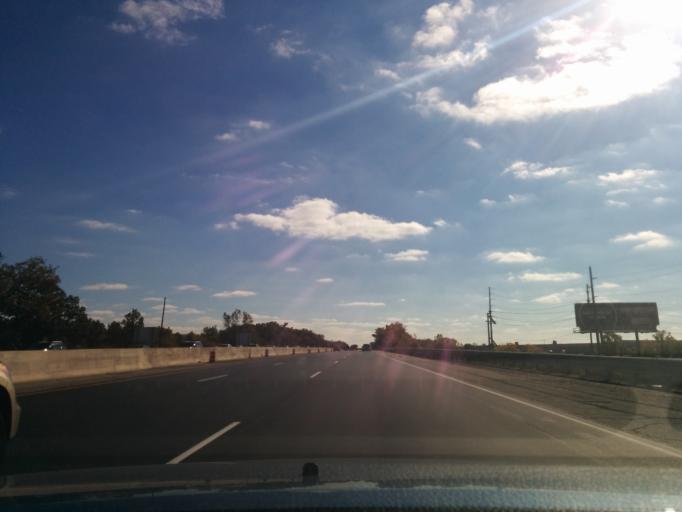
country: US
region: Michigan
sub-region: Oakland County
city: South Lyon
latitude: 42.5164
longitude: -83.6075
